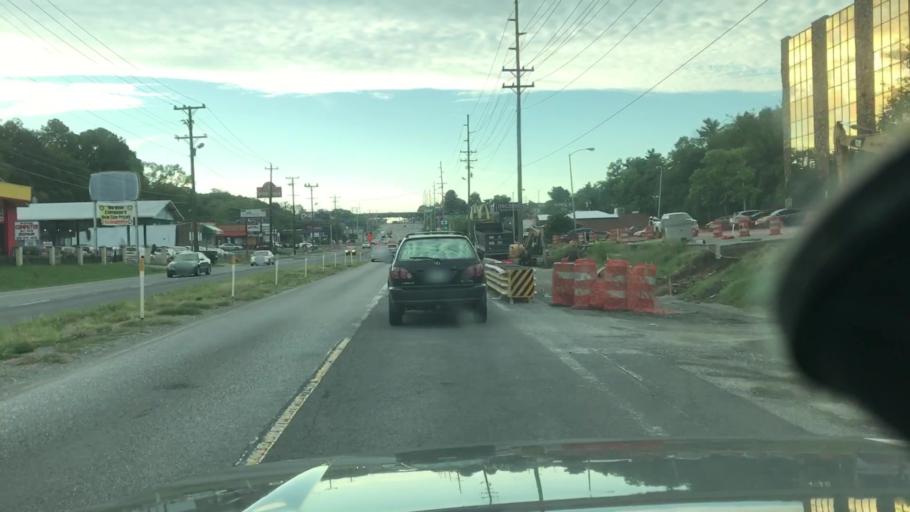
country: US
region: Tennessee
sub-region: Davidson County
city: Oak Hill
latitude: 36.1234
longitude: -86.7069
